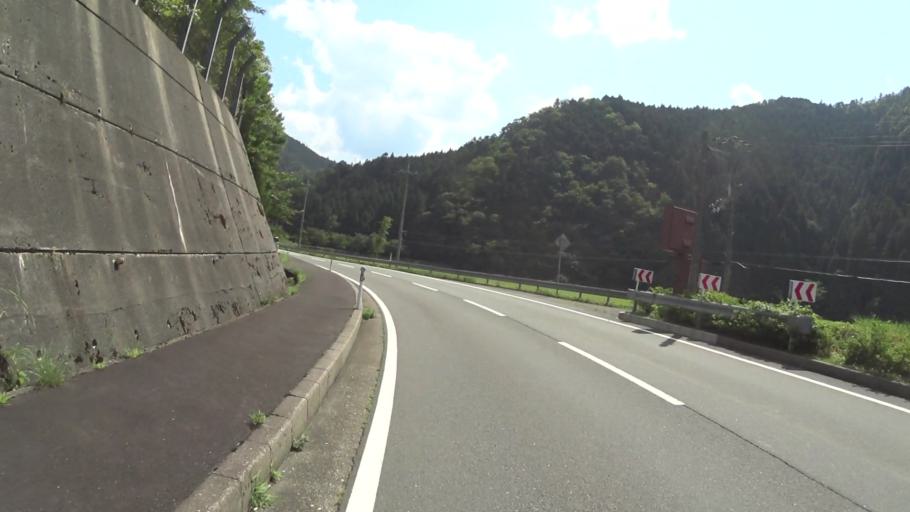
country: JP
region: Fukui
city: Obama
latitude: 35.3266
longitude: 135.5658
